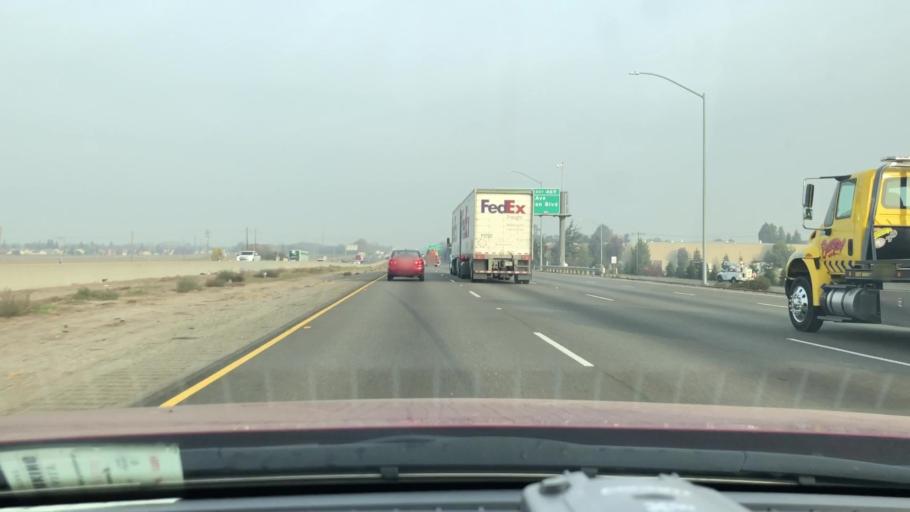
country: US
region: California
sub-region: San Joaquin County
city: Taft Mosswood
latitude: 37.8977
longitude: -121.2840
